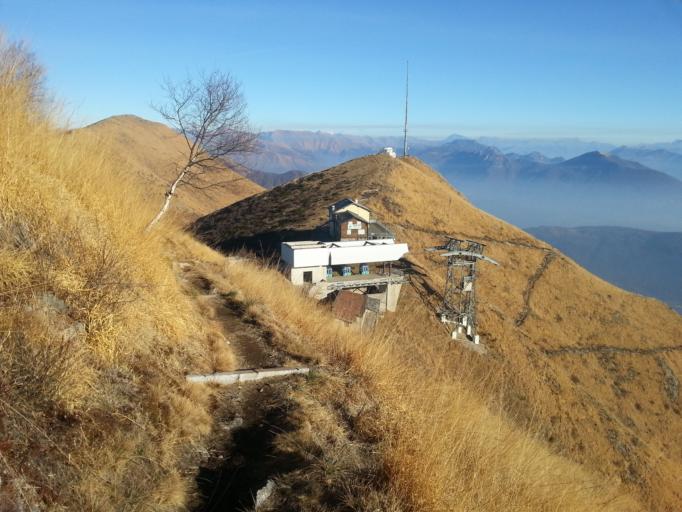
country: IT
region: Lombardy
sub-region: Provincia di Varese
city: Curiglia
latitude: 46.0404
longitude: 8.8332
